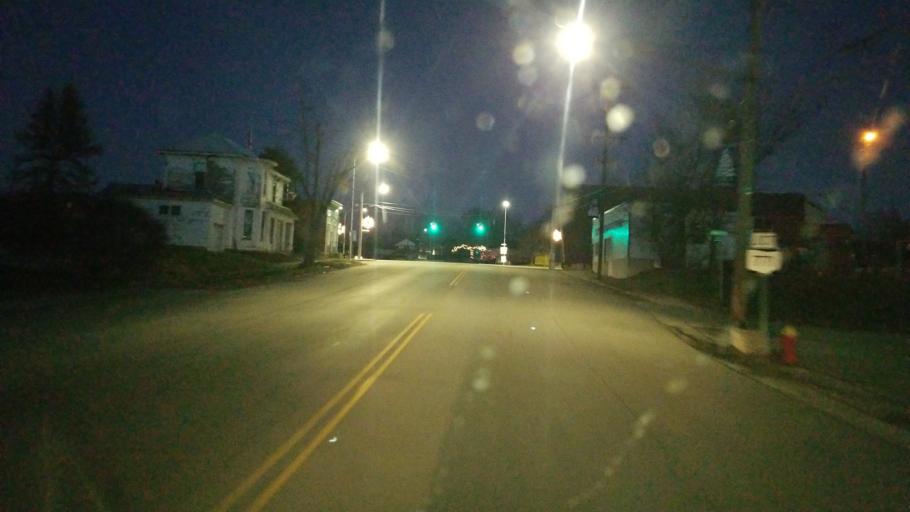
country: US
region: Ohio
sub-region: Highland County
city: Leesburg
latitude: 39.3453
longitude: -83.5564
